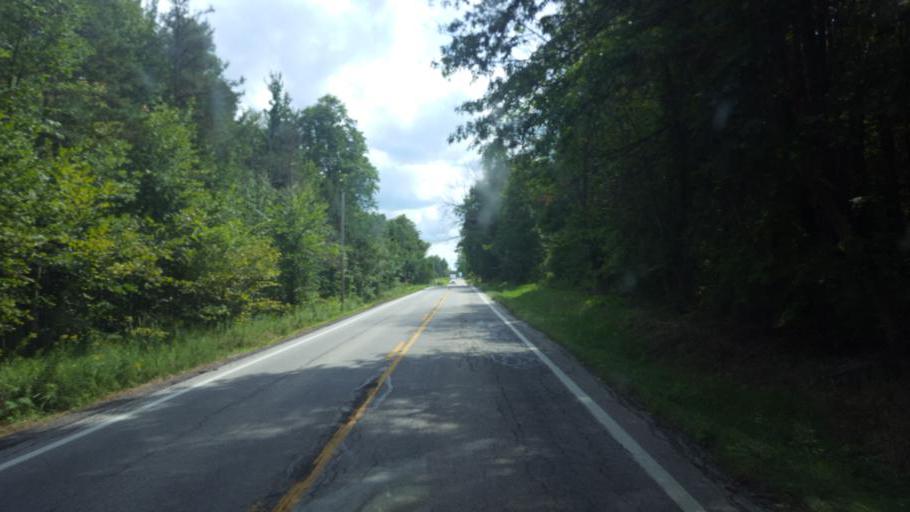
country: US
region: Ohio
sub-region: Portage County
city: Hiram
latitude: 41.3585
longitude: -81.1431
